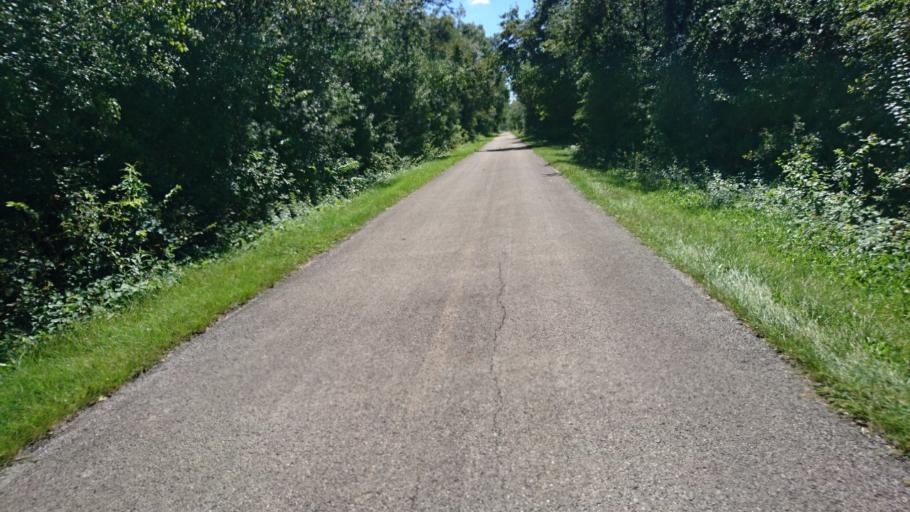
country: US
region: Illinois
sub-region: Cook County
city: Glenwood
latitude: 41.5443
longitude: -87.6238
